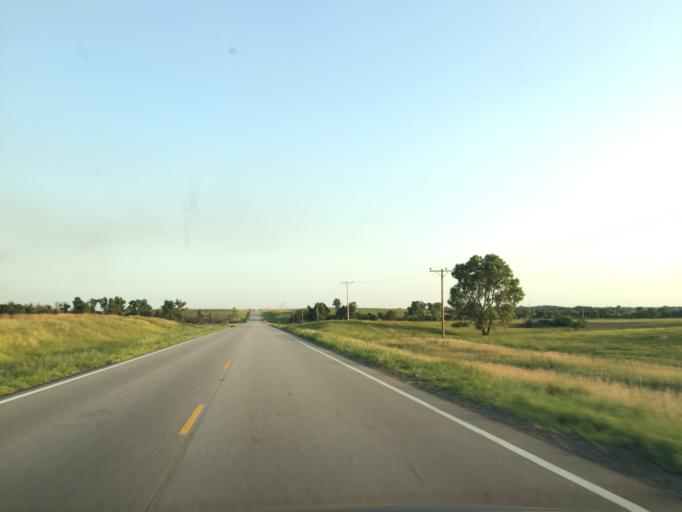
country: US
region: Kansas
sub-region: Ellsworth County
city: Ellsworth
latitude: 38.6851
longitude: -98.2022
